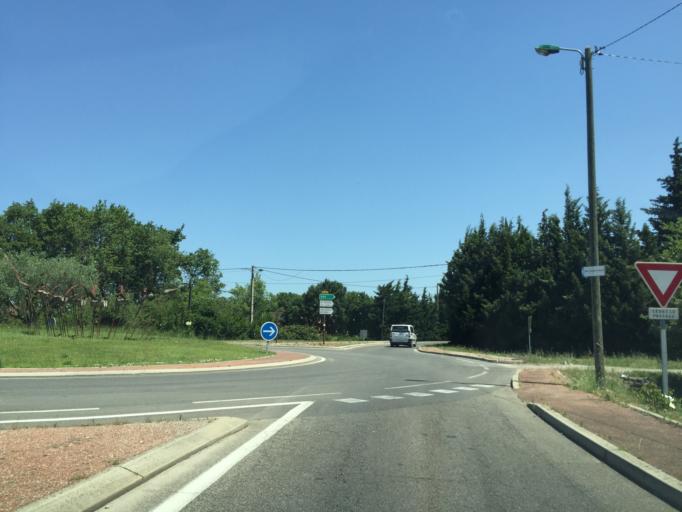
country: FR
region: Provence-Alpes-Cote d'Azur
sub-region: Departement du Vaucluse
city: Serignan-du-Comtat
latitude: 44.1911
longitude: 4.8582
